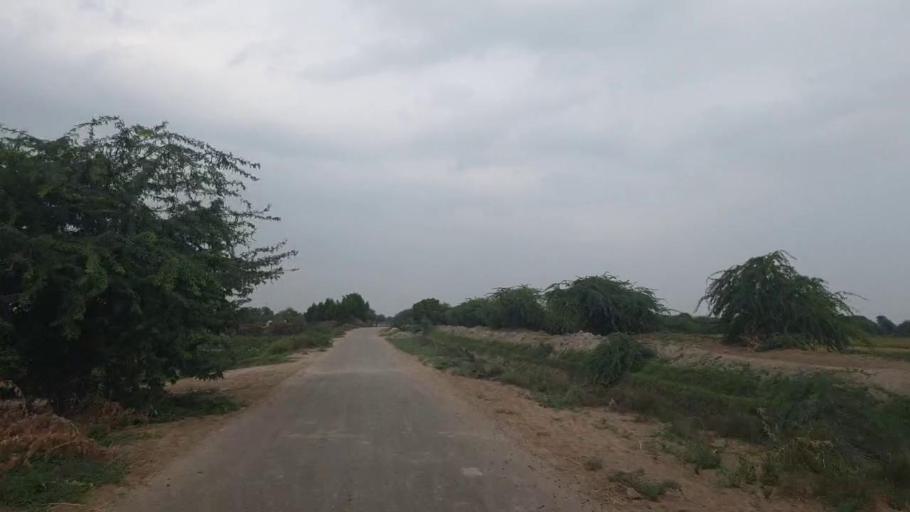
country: PK
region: Sindh
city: Badin
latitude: 24.6200
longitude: 68.6817
